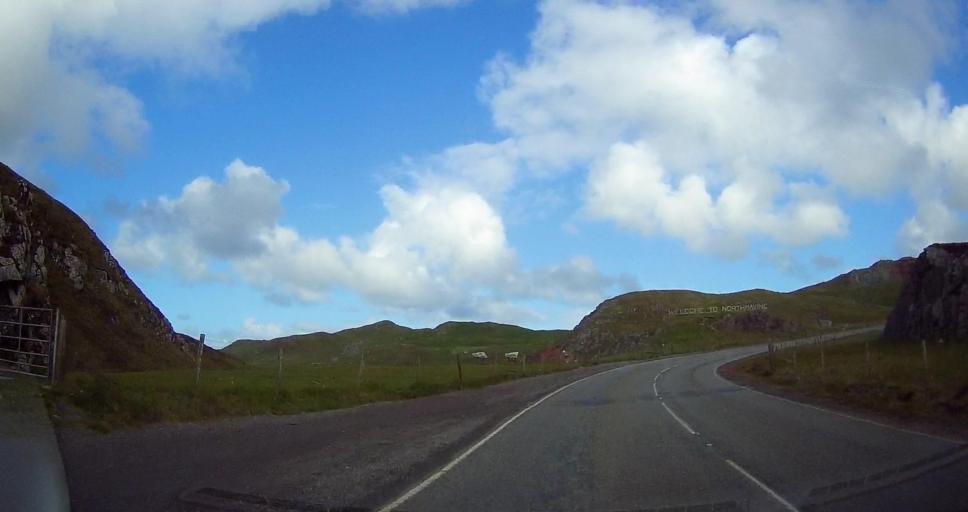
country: GB
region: Scotland
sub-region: Shetland Islands
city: Lerwick
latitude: 60.3972
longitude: -1.3837
